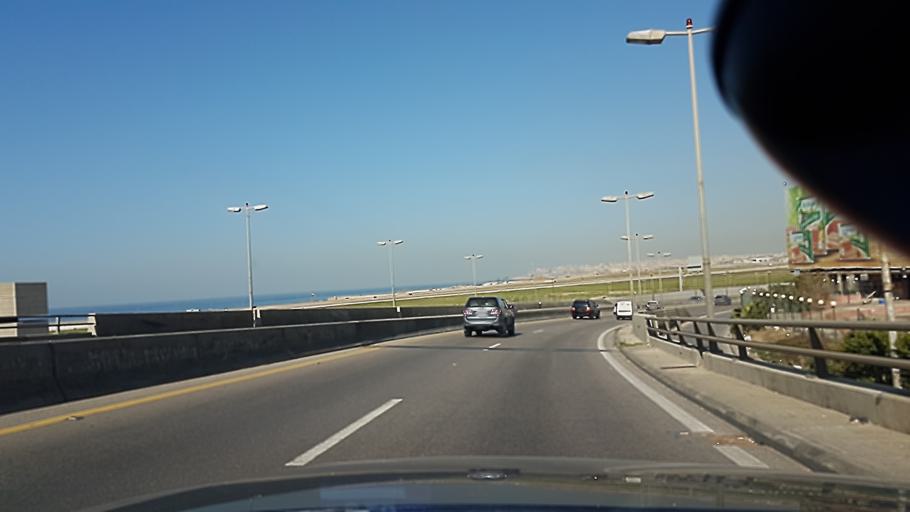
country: LB
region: Mont-Liban
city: Baabda
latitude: 33.7963
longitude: 35.4826
